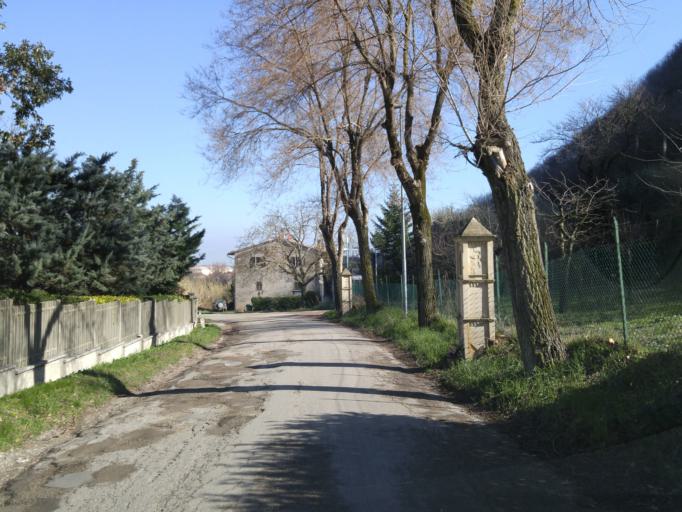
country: IT
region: The Marches
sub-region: Provincia di Pesaro e Urbino
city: Fossombrone
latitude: 43.6812
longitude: 12.8026
